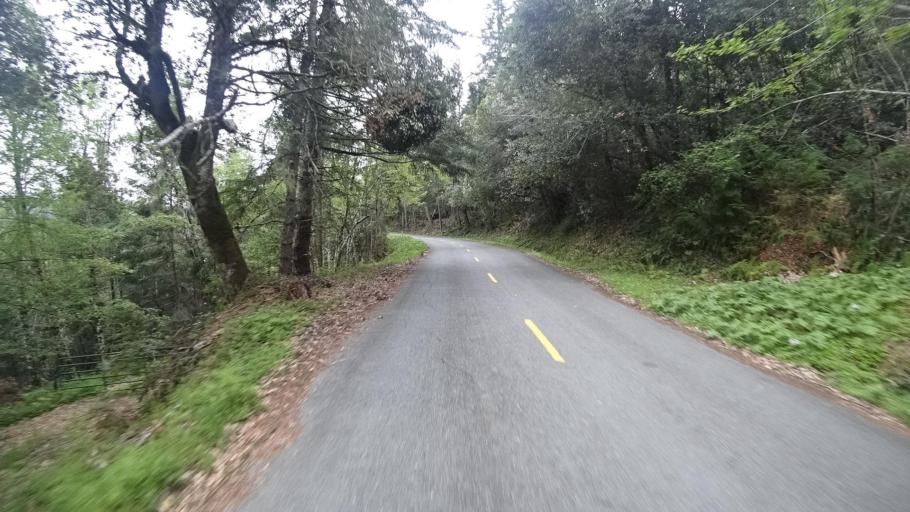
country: US
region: California
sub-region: Humboldt County
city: Blue Lake
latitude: 40.9327
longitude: -123.8464
